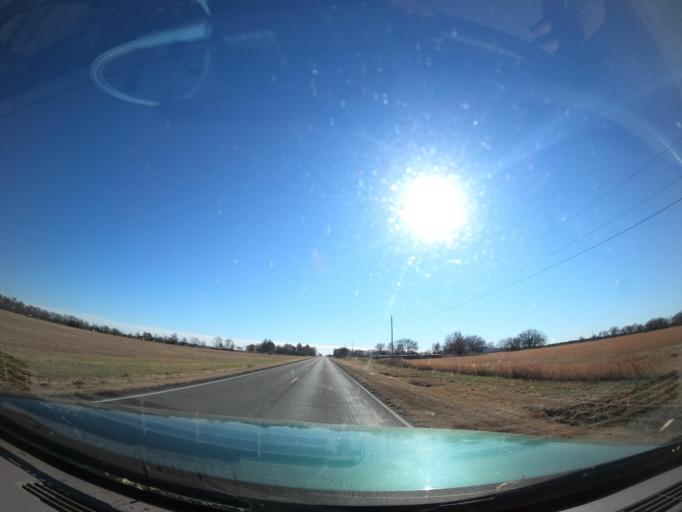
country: US
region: Oklahoma
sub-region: Muskogee County
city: Haskell
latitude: 35.6955
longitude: -95.6423
